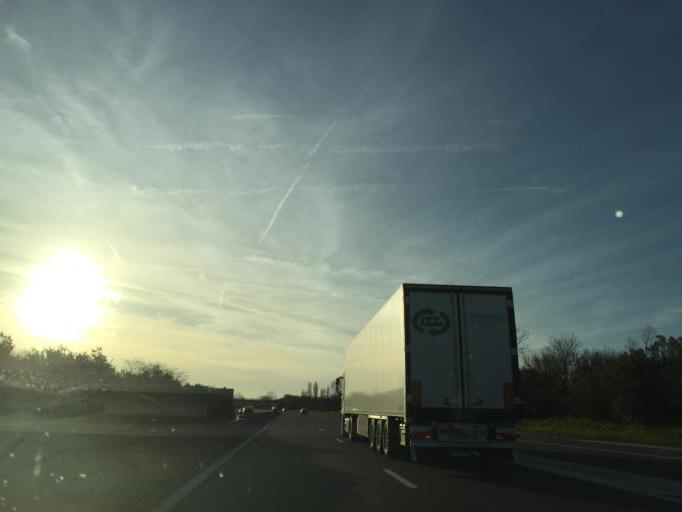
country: FR
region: Rhone-Alpes
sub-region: Departement du Rhone
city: Marennes
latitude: 45.6434
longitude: 4.9044
